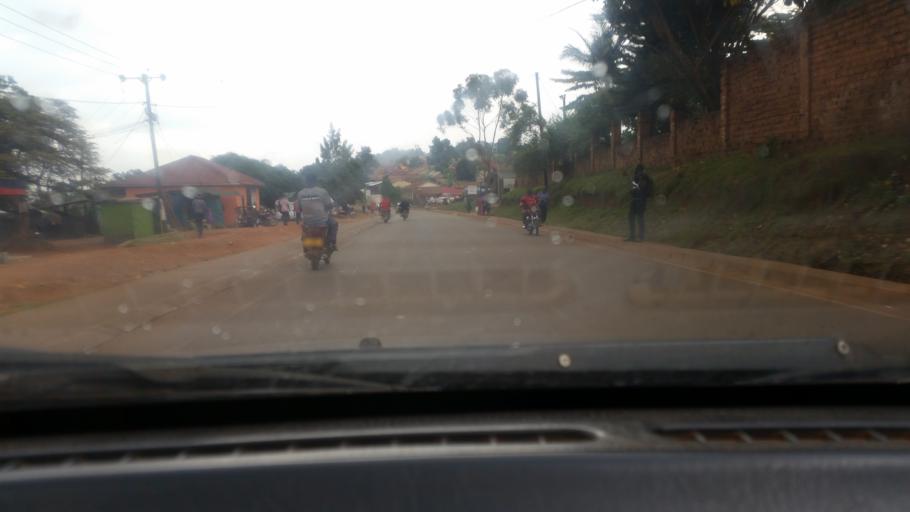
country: UG
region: Central Region
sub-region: Wakiso District
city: Kireka
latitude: 0.3539
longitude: 32.6506
